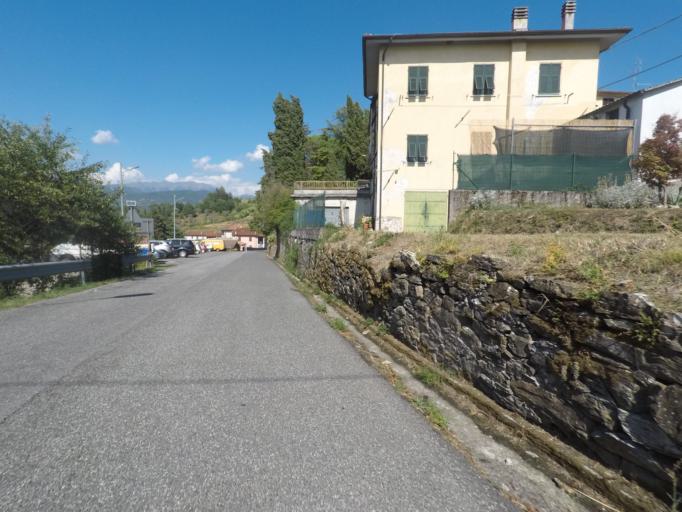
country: IT
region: Tuscany
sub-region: Provincia di Massa-Carrara
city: Pallerone
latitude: 44.1919
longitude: 10.0534
